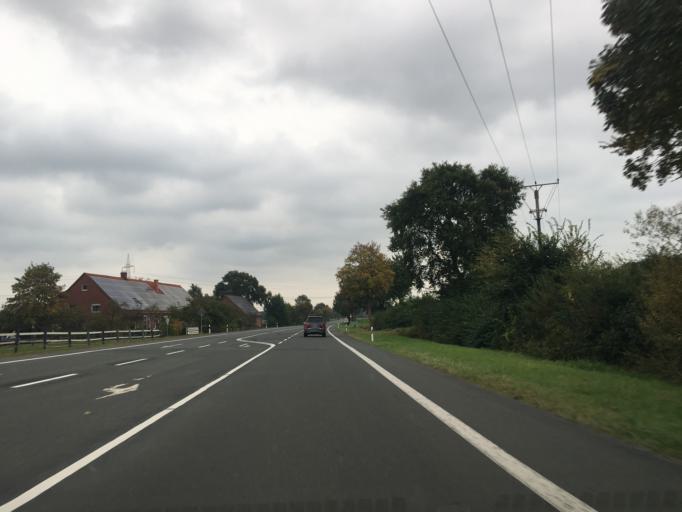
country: DE
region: North Rhine-Westphalia
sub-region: Regierungsbezirk Munster
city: Steinfurt
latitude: 52.1462
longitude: 7.4054
